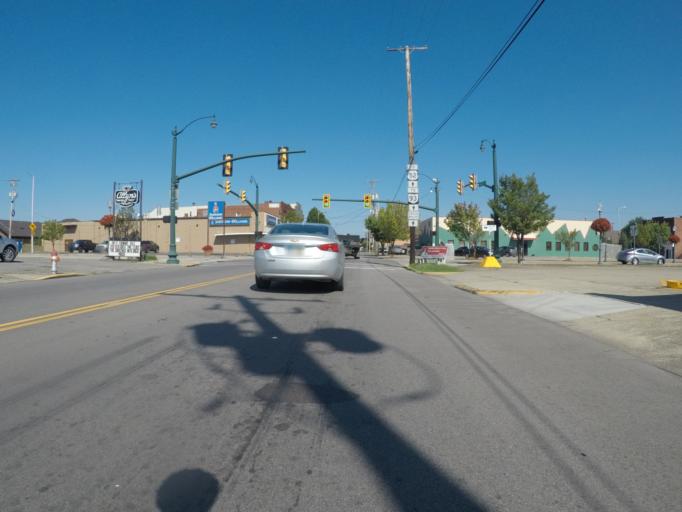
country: US
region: Ohio
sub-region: Lawrence County
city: Ironton
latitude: 38.5317
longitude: -82.6835
